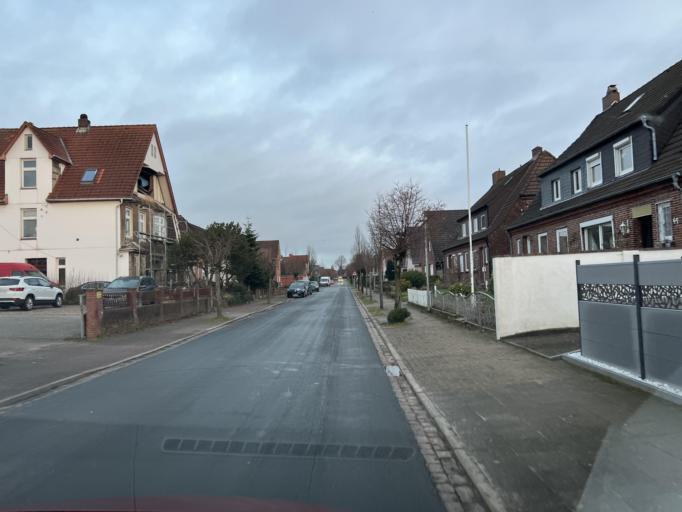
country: DE
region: Schleswig-Holstein
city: Wesseln
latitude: 54.1954
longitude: 9.0830
